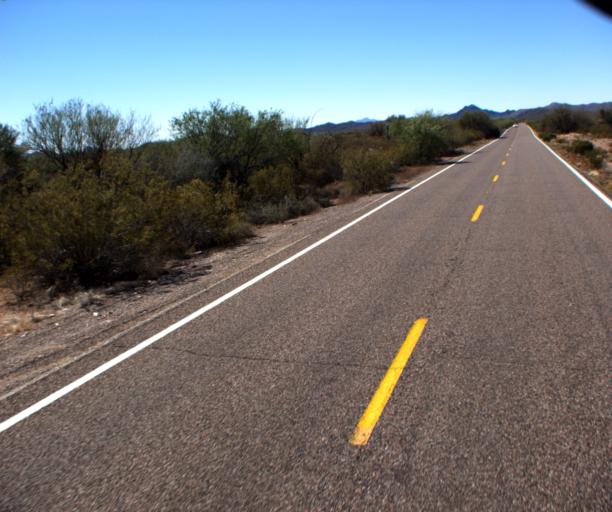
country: MX
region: Sonora
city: Sonoyta
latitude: 32.0404
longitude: -112.7954
